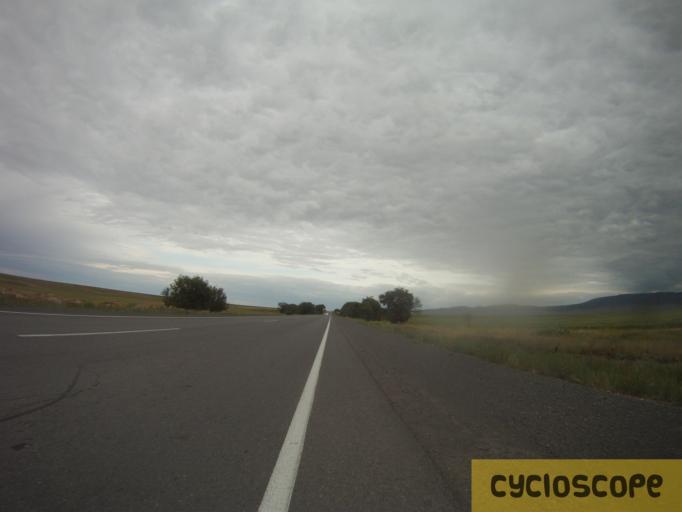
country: KG
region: Chuy
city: Tokmok
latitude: 43.3633
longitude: 75.3609
